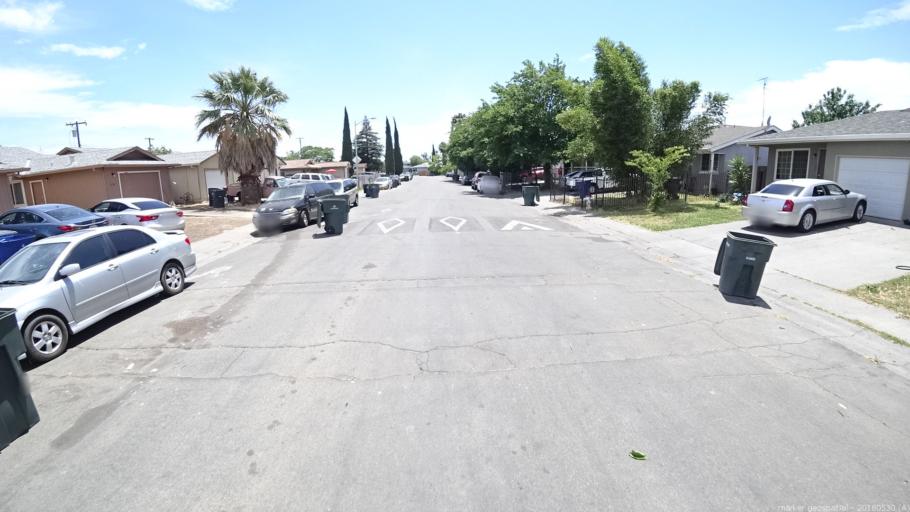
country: US
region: California
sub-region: Sacramento County
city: Sacramento
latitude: 38.6234
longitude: -121.4674
